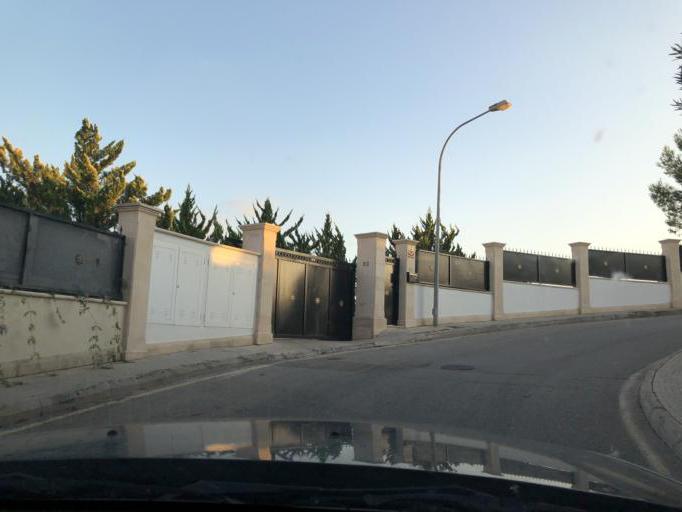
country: ES
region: Balearic Islands
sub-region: Illes Balears
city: Santa Ponsa
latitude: 39.5267
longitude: 2.4636
